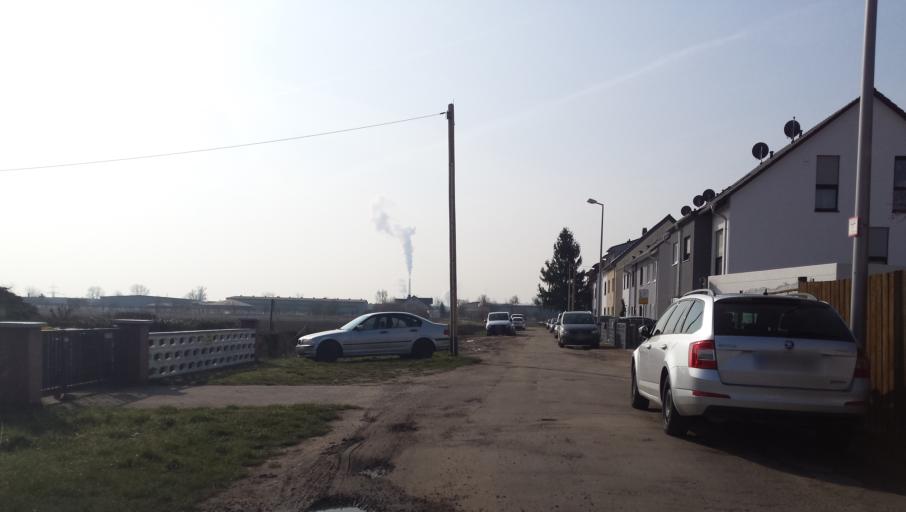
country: DE
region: Hesse
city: Lampertheim
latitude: 49.5618
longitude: 8.4499
